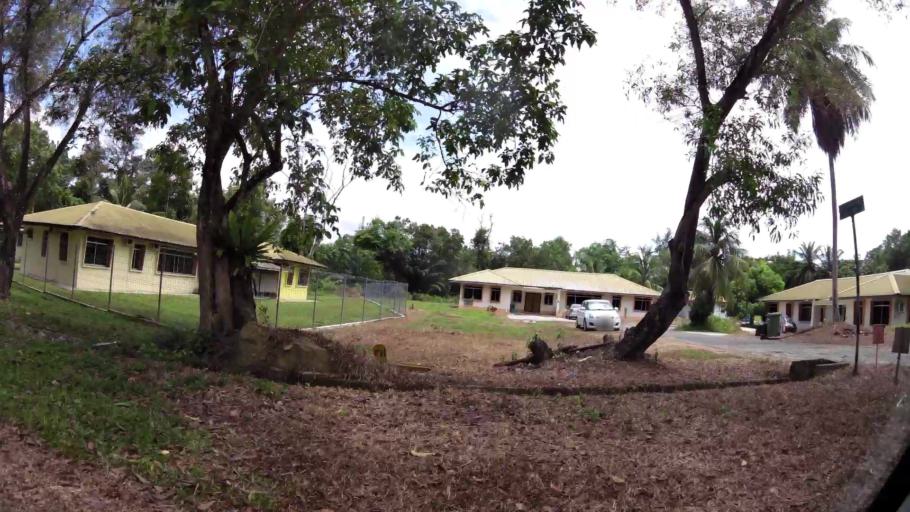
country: BN
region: Brunei and Muara
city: Bandar Seri Begawan
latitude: 4.9013
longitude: 114.9113
